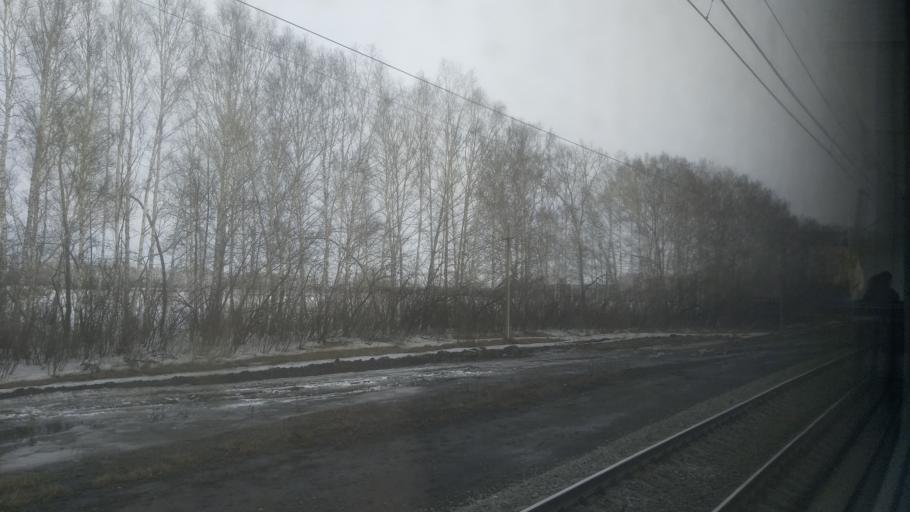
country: RU
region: Novosibirsk
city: Bolotnoye
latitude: 55.7092
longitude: 84.6148
